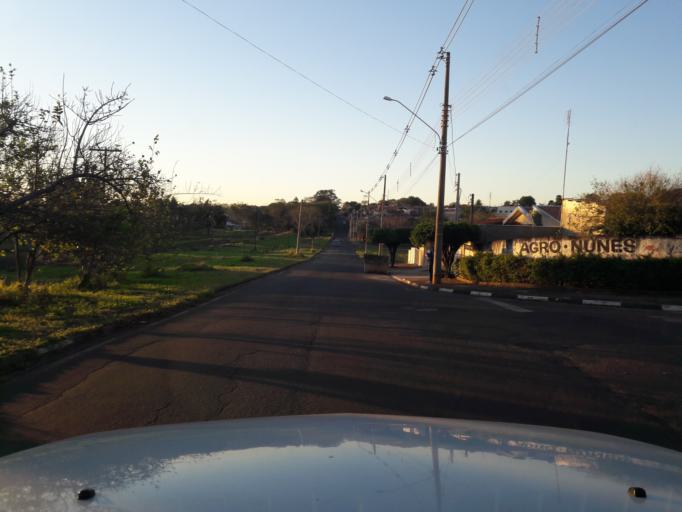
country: BR
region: Sao Paulo
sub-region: Moji-Guacu
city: Mogi-Gaucu
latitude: -22.3437
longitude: -46.9344
